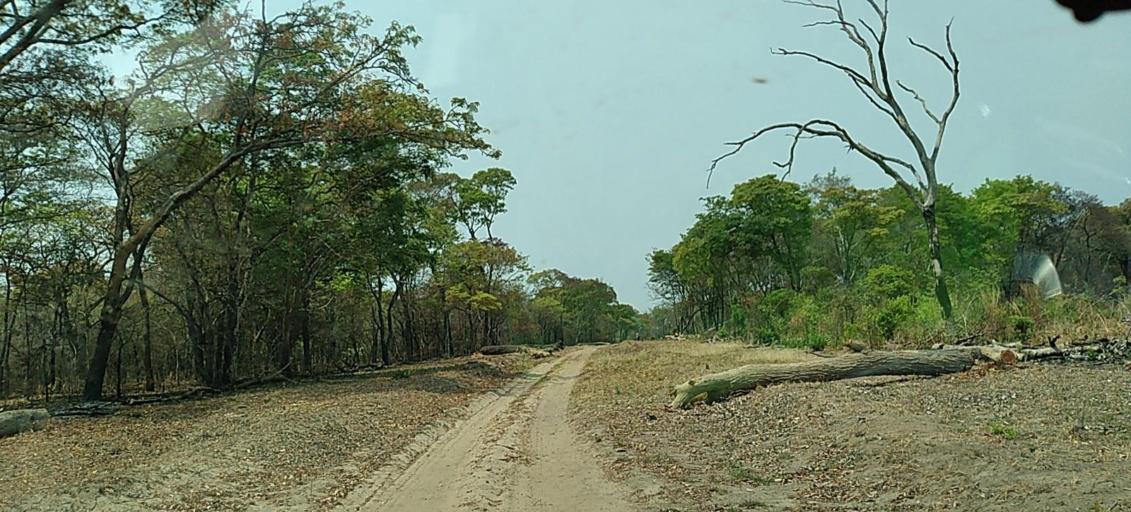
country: ZM
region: Western
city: Lukulu
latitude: -13.9562
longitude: 23.2247
